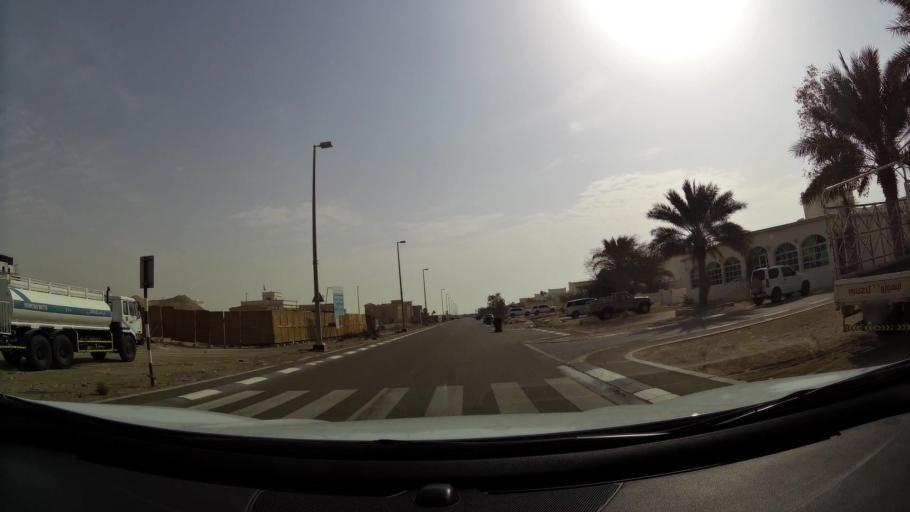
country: AE
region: Abu Dhabi
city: Abu Dhabi
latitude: 24.2771
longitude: 54.6917
